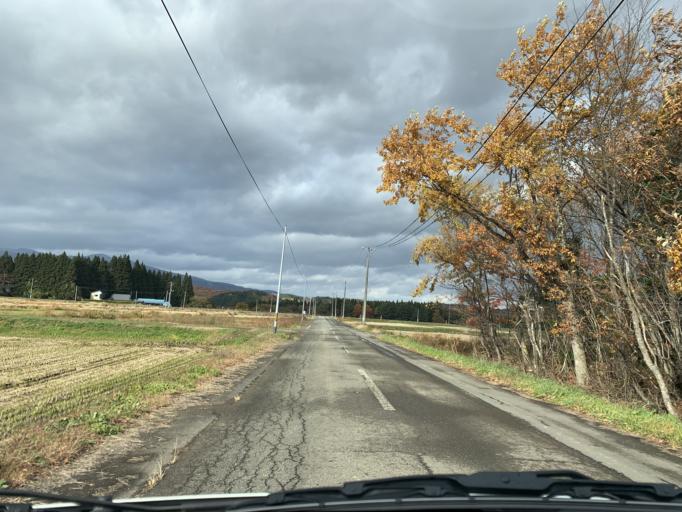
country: JP
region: Iwate
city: Mizusawa
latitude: 39.1159
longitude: 140.9733
